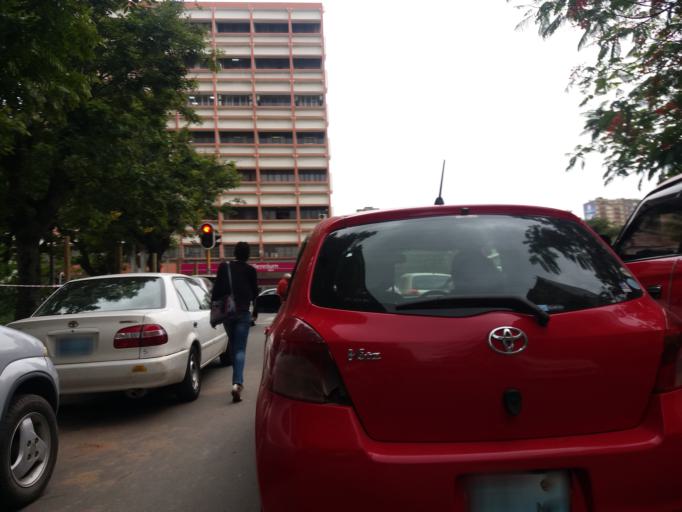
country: MZ
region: Maputo City
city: Maputo
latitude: -25.9671
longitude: 32.5752
